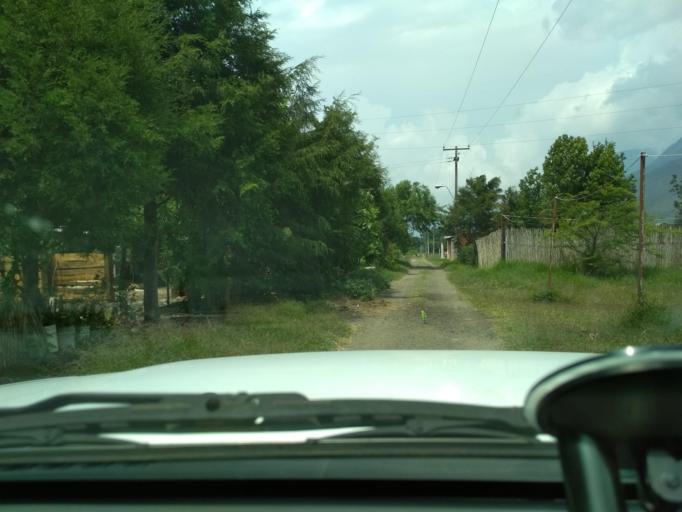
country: MX
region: Veracruz
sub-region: Nogales
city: Taza de Agua Ojo Zarco
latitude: 18.7804
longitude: -97.2154
